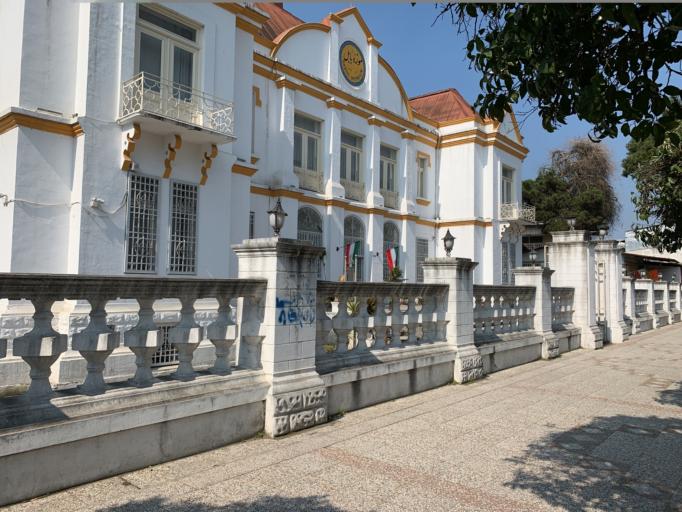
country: IR
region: Mazandaran
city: Babol
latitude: 36.5445
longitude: 52.6766
